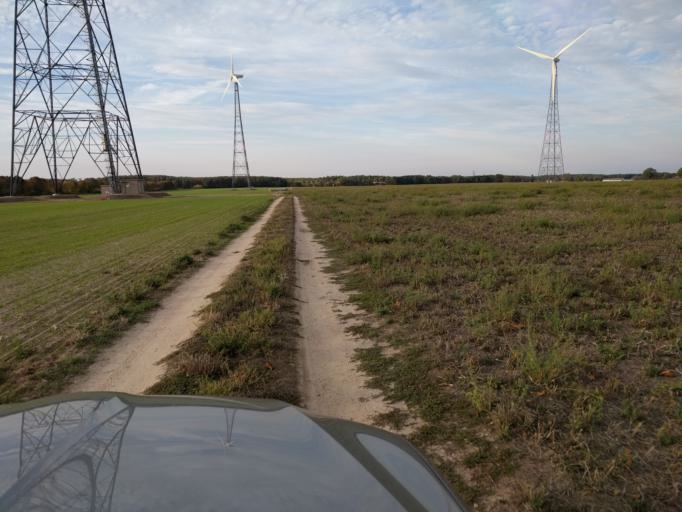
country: DE
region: Brandenburg
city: Ziesar
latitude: 52.2008
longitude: 12.2819
